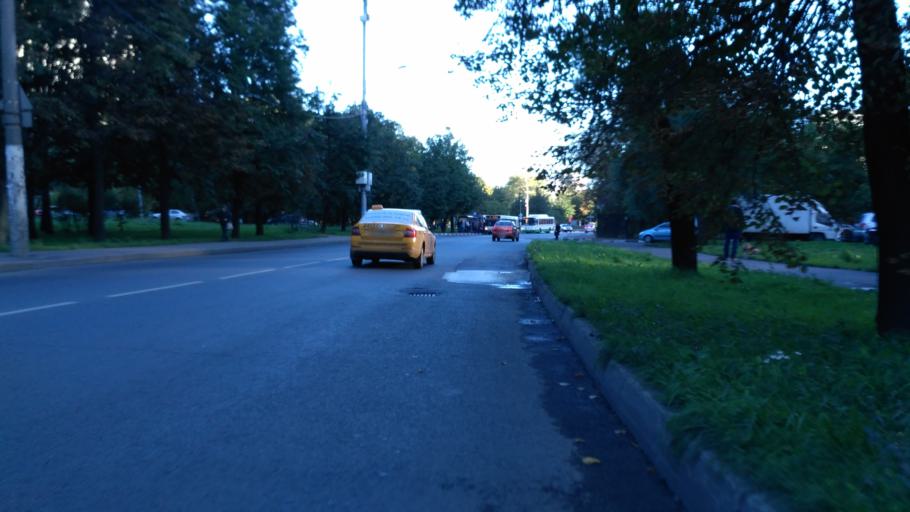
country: RU
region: Moscow
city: Zapadnoye Degunino
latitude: 55.8747
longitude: 37.5348
